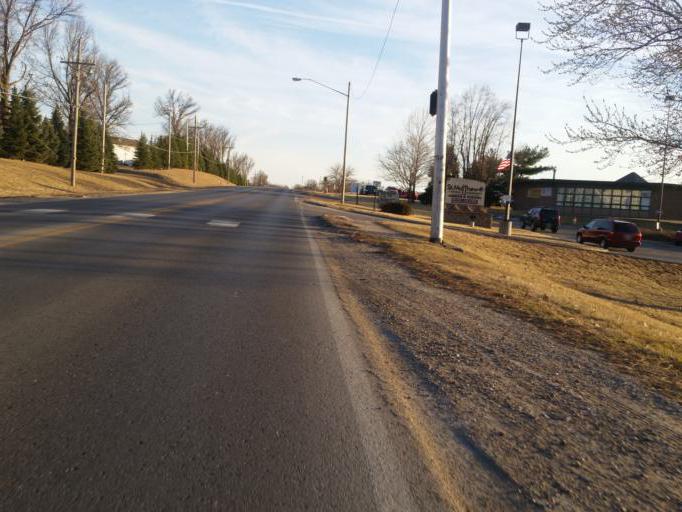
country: US
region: Nebraska
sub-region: Sarpy County
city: Offutt Air Force Base
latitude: 41.1265
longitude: -95.9666
